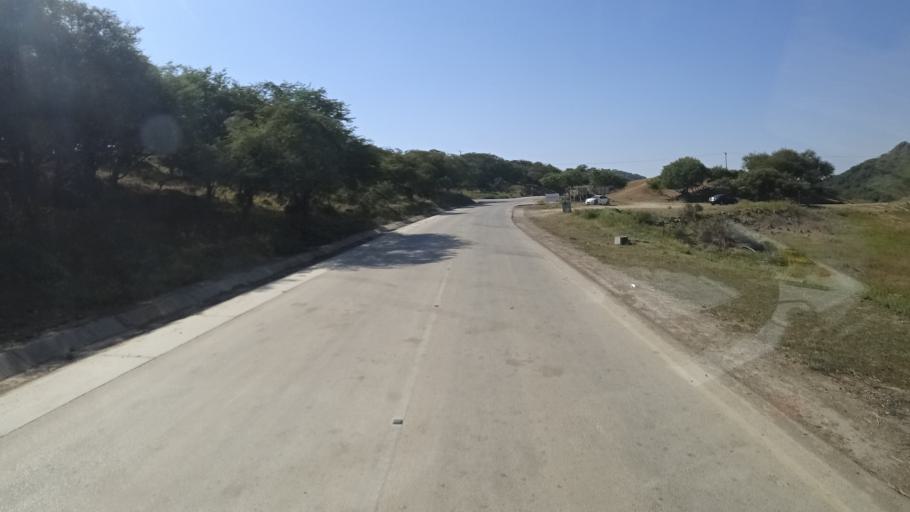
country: OM
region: Zufar
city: Salalah
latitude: 17.0660
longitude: 54.5983
